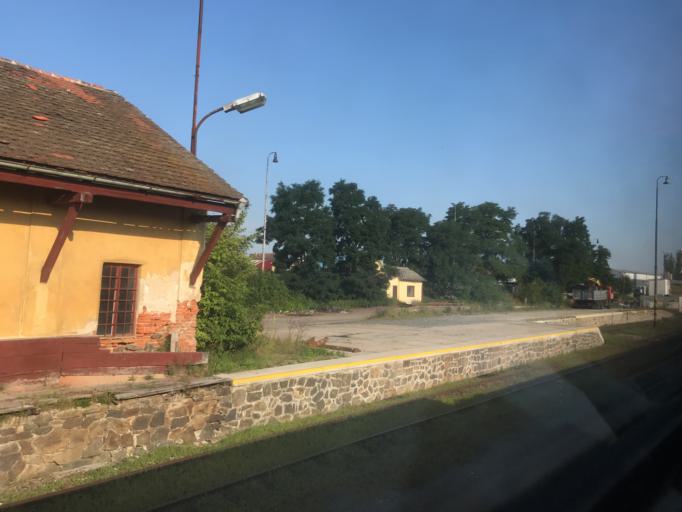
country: CZ
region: Jihocesky
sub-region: Okres Jindrichuv Hradec
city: Trebon
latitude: 49.0161
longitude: 14.7602
